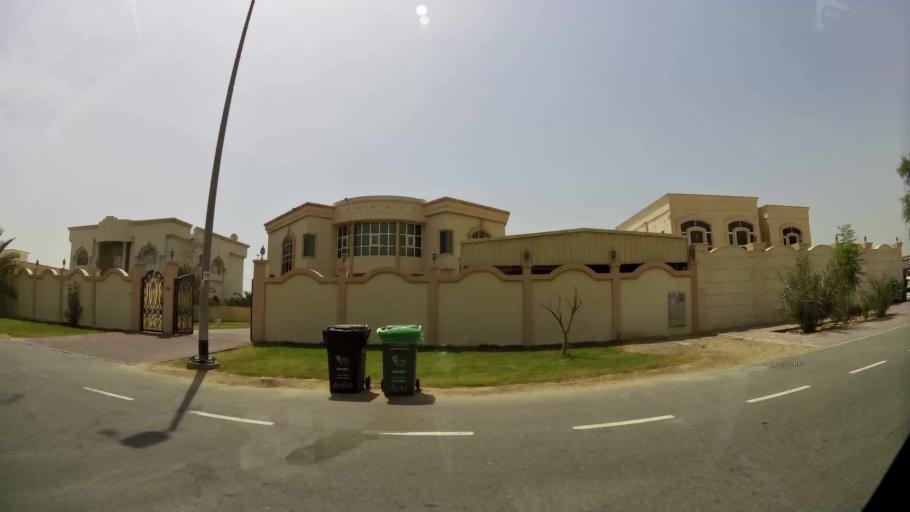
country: AE
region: Ash Shariqah
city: Sharjah
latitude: 25.2410
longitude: 55.4282
